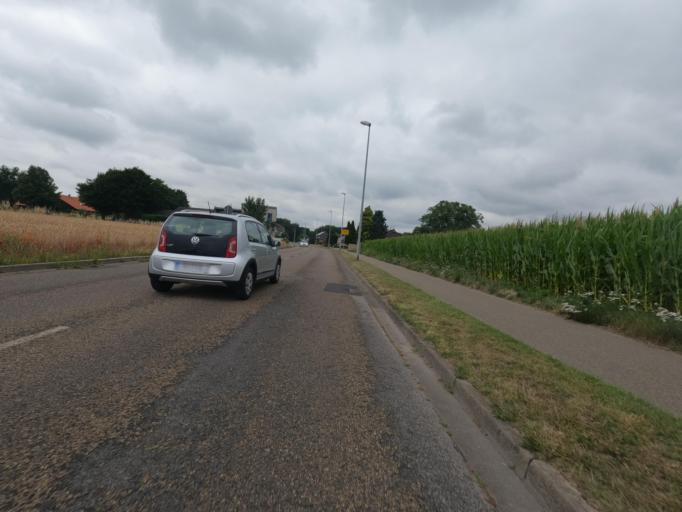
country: DE
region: North Rhine-Westphalia
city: Geilenkirchen
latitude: 50.9775
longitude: 6.1096
